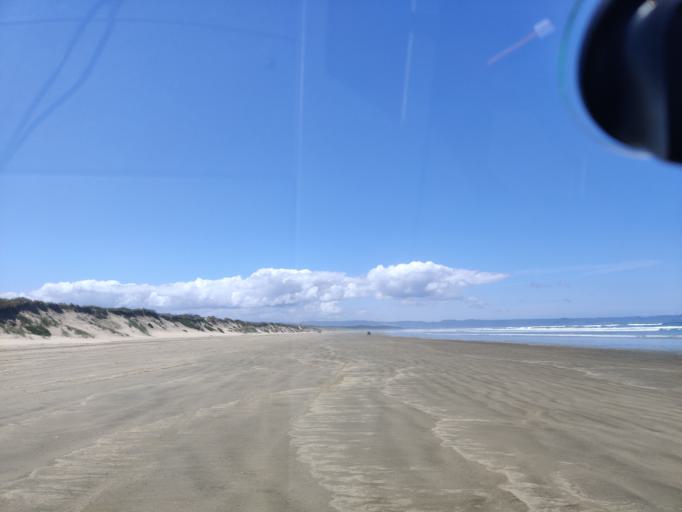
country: NZ
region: Northland
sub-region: Far North District
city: Kaitaia
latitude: -35.0317
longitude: 173.1648
